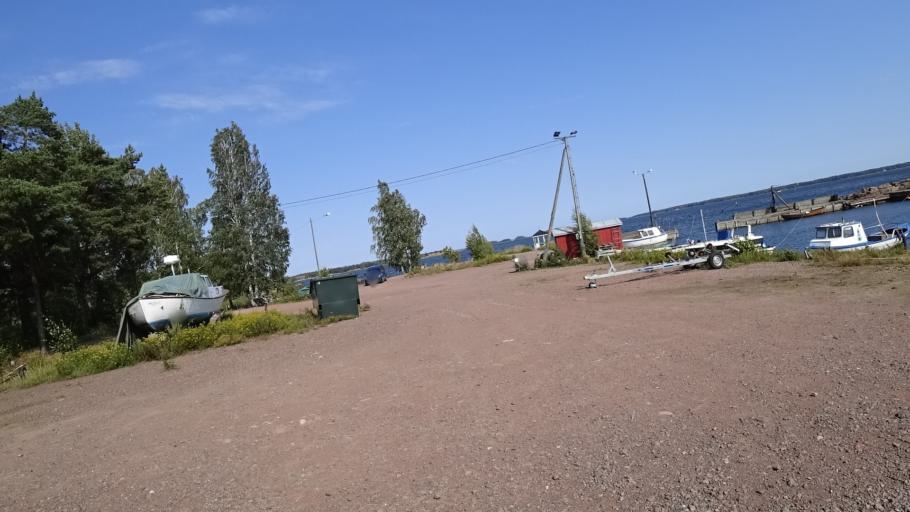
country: FI
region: Kymenlaakso
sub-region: Kotka-Hamina
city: Kotka
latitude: 60.4495
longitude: 26.9457
